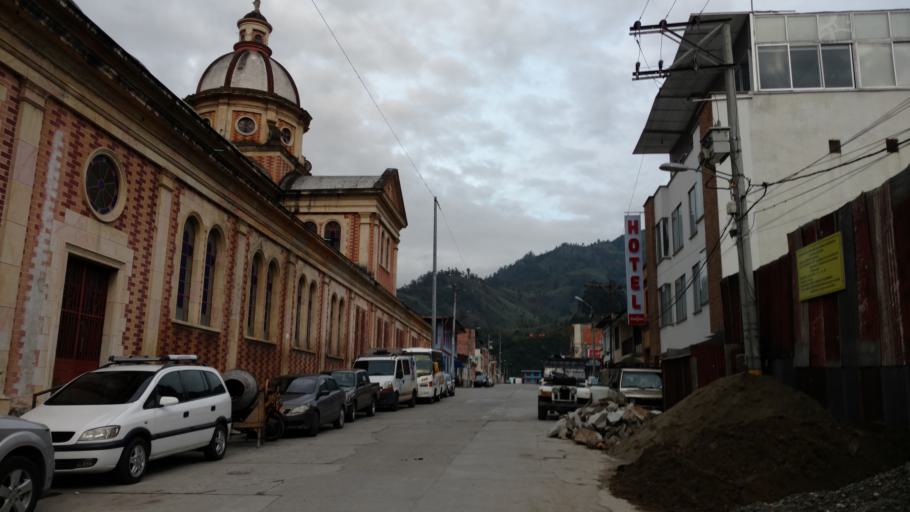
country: CO
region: Tolima
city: Cajamarca
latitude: 4.4424
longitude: -75.4273
